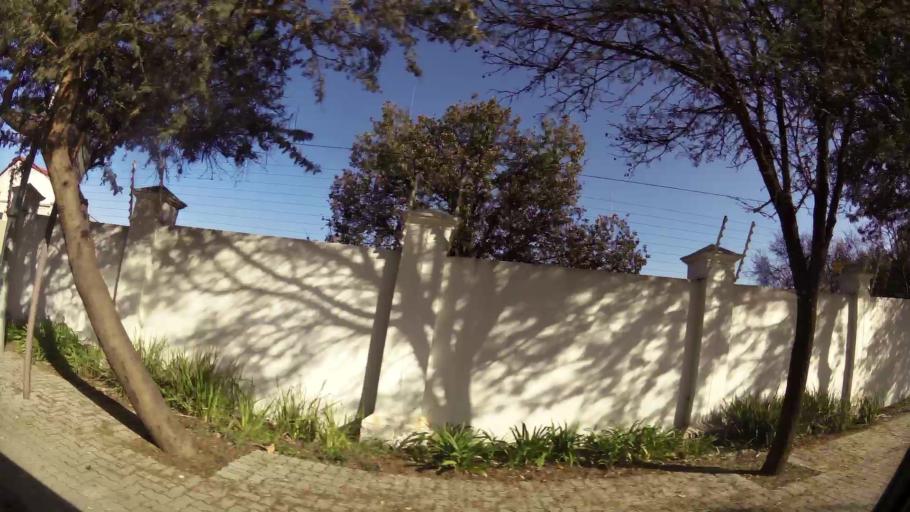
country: ZA
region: Gauteng
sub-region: City of Johannesburg Metropolitan Municipality
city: Diepsloot
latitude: -26.0207
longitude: 27.9940
